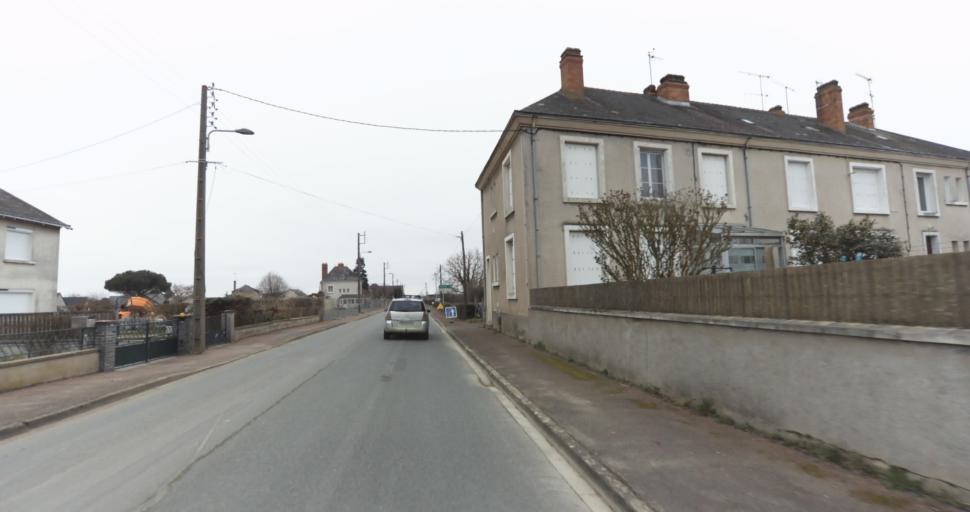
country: FR
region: Pays de la Loire
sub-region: Departement de Maine-et-Loire
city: Montreuil-Bellay
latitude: 47.1255
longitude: -0.1464
